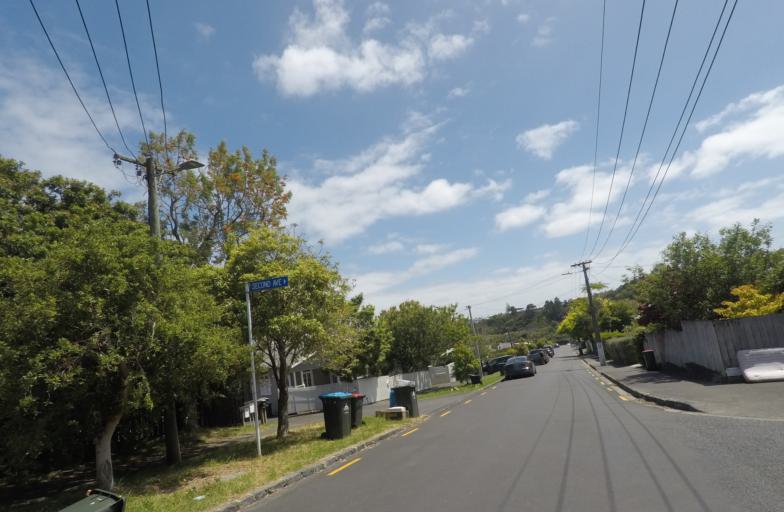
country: NZ
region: Auckland
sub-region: Auckland
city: Auckland
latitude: -36.8716
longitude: 174.7377
